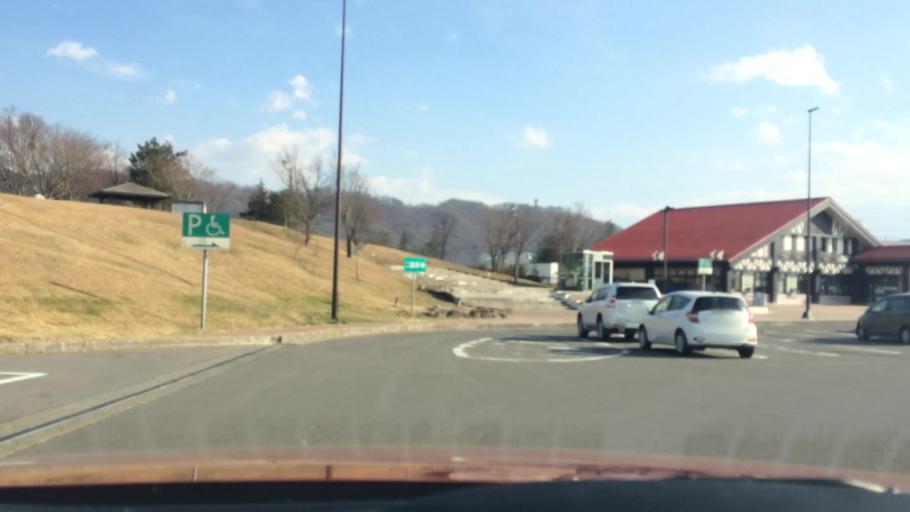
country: JP
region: Nagano
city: Toyoshina
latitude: 36.2717
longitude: 137.9314
